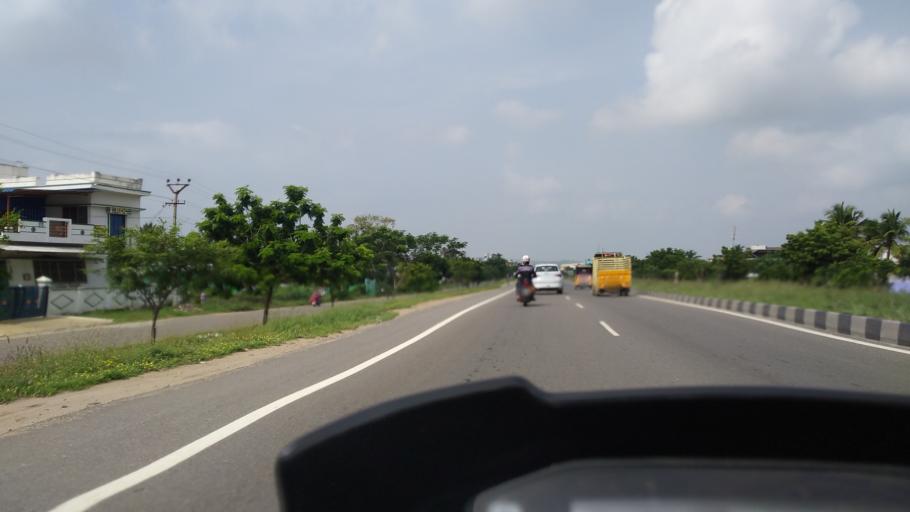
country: IN
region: Tamil Nadu
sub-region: Erode
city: Bhavani
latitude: 11.4354
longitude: 77.7027
